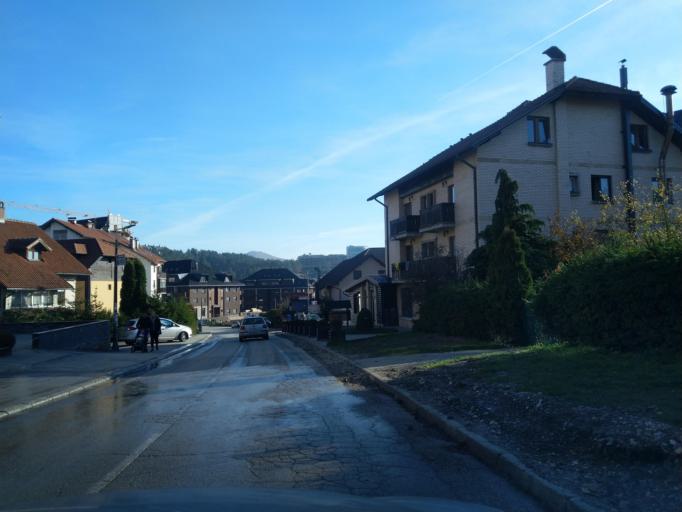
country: RS
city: Zlatibor
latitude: 43.7265
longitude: 19.6914
